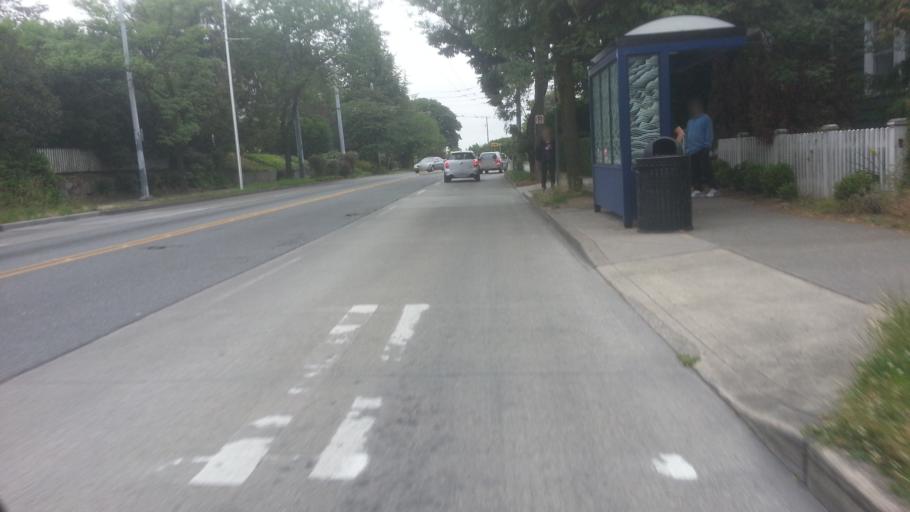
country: US
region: Washington
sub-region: King County
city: Seattle
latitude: 47.6268
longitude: -122.3023
